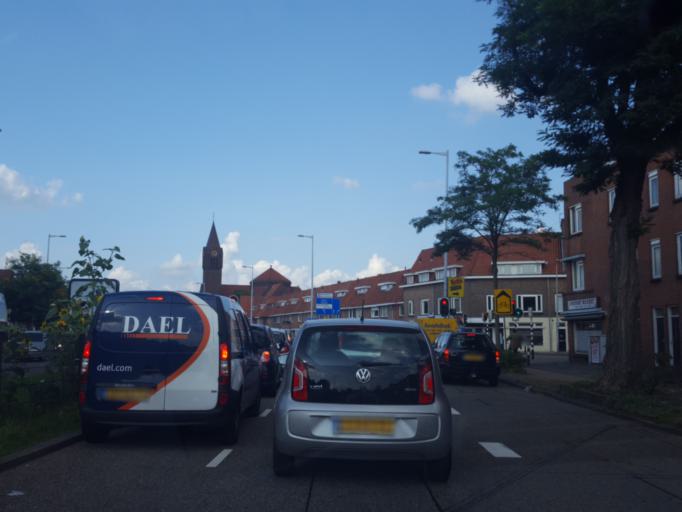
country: NL
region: Utrecht
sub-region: Gemeente Utrecht
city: Utrecht
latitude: 52.0932
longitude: 5.0850
